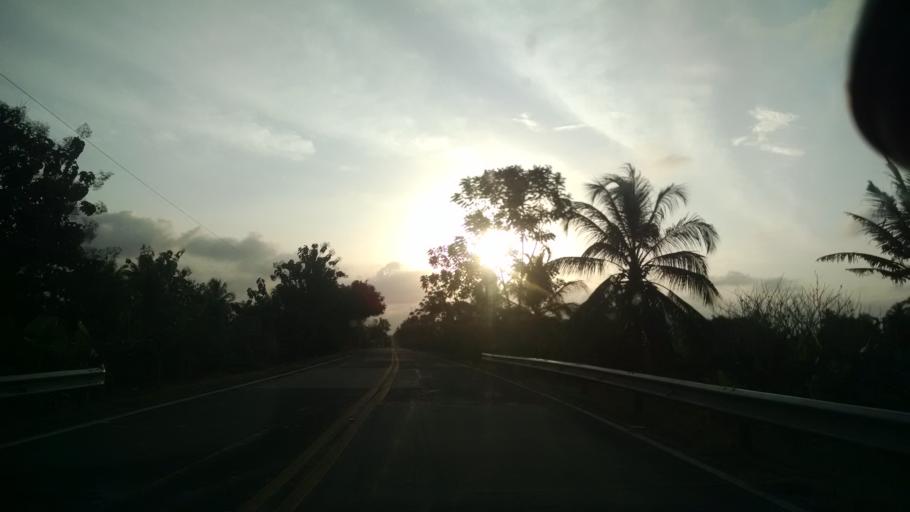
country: CO
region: Antioquia
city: San Juan de Uraba
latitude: 8.7328
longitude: -76.5784
